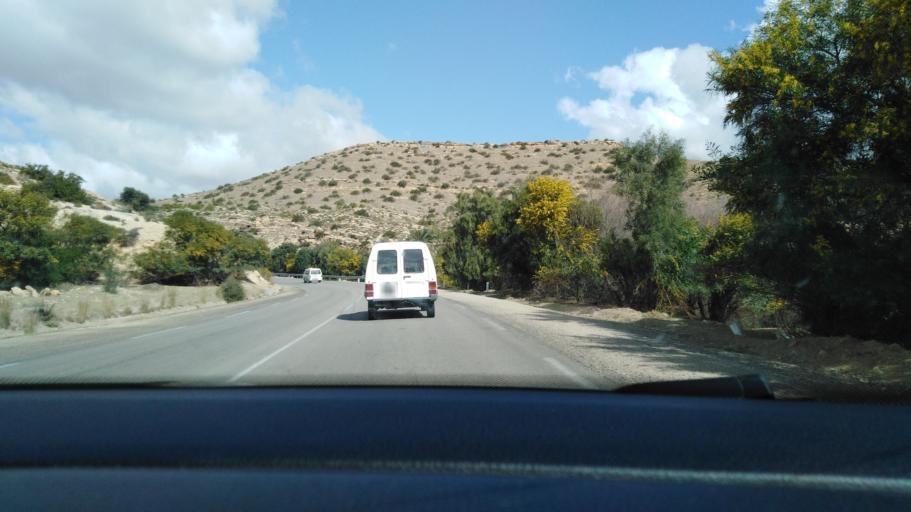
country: TN
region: Al Qayrawan
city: Haffouz
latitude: 35.6330
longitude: 9.8223
